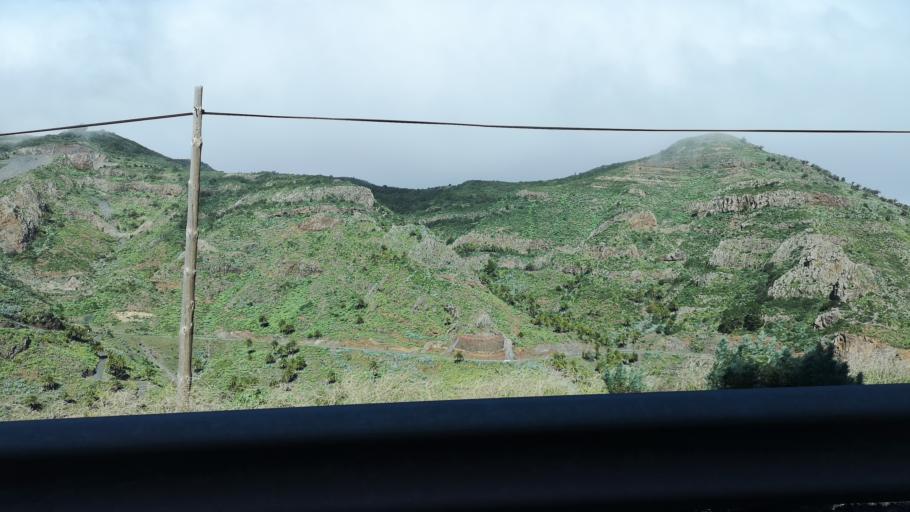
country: ES
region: Canary Islands
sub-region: Provincia de Santa Cruz de Tenerife
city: Alajero
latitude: 28.0907
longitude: -17.2007
